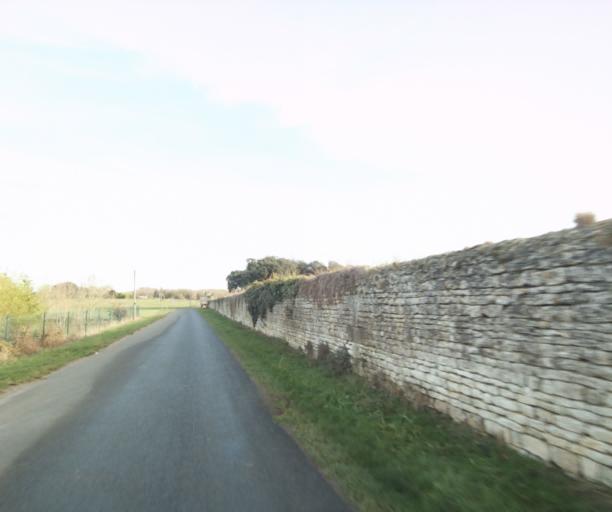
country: FR
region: Poitou-Charentes
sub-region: Departement de la Charente-Maritime
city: Saint-Hilaire-de-Villefranche
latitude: 45.8219
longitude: -0.5635
